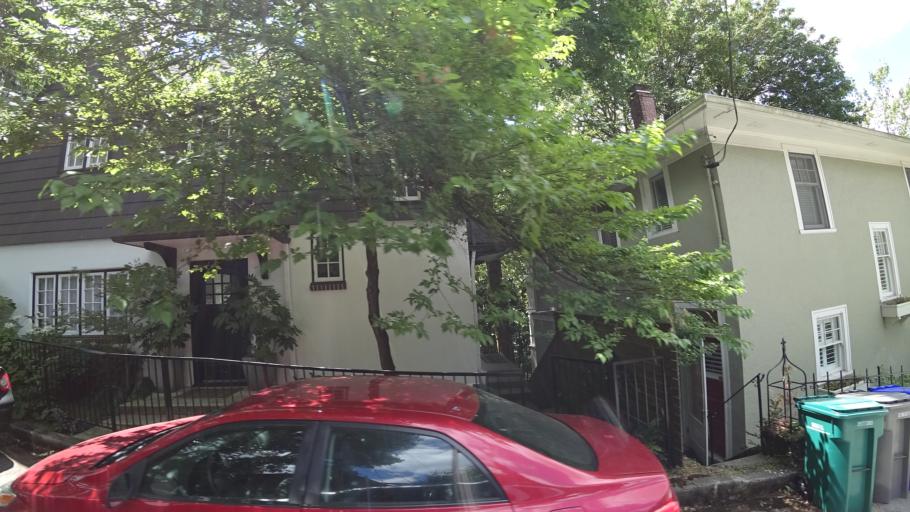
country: US
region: Oregon
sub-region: Multnomah County
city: Portland
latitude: 45.5184
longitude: -122.6993
